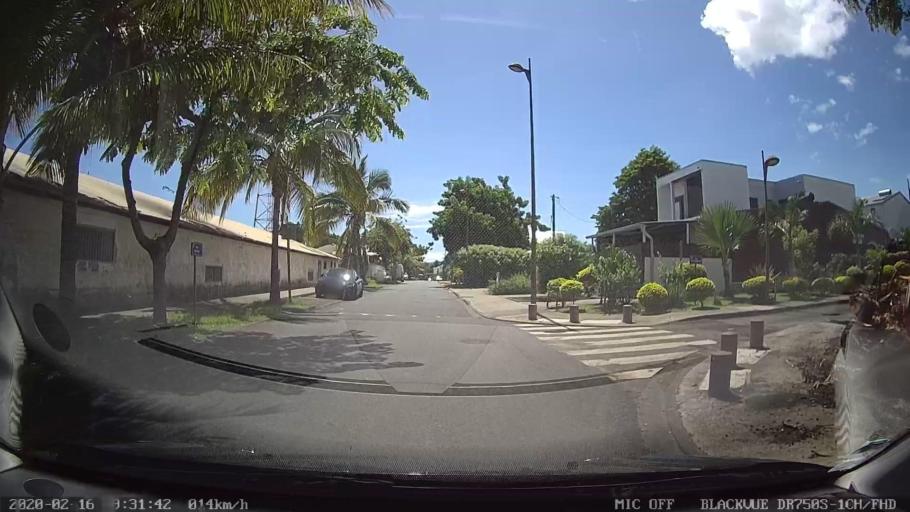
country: RE
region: Reunion
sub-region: Reunion
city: Saint-Denis
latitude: -20.8794
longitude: 55.4406
